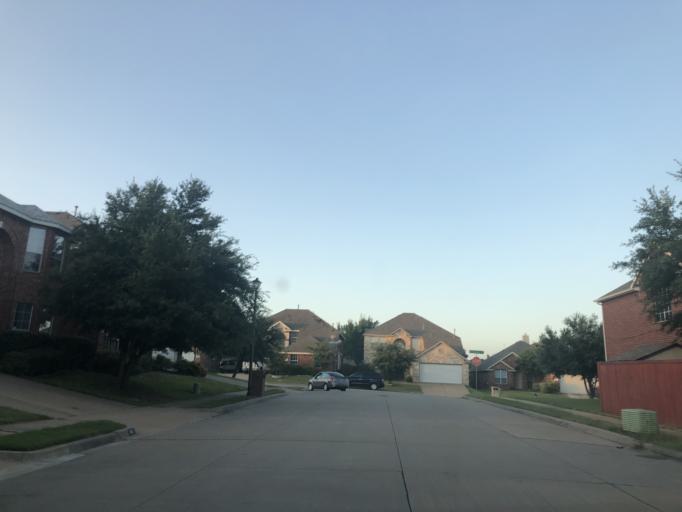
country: US
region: Texas
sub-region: Dallas County
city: Duncanville
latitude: 32.6558
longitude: -96.9618
